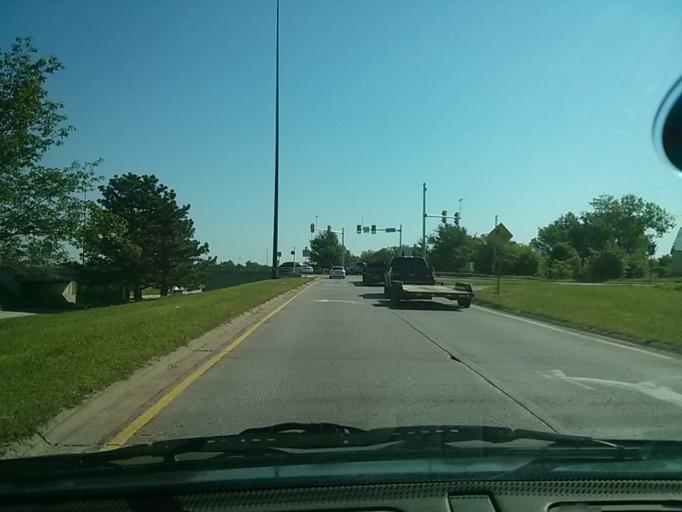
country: US
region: Oklahoma
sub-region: Tulsa County
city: Tulsa
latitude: 36.1743
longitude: -95.9763
